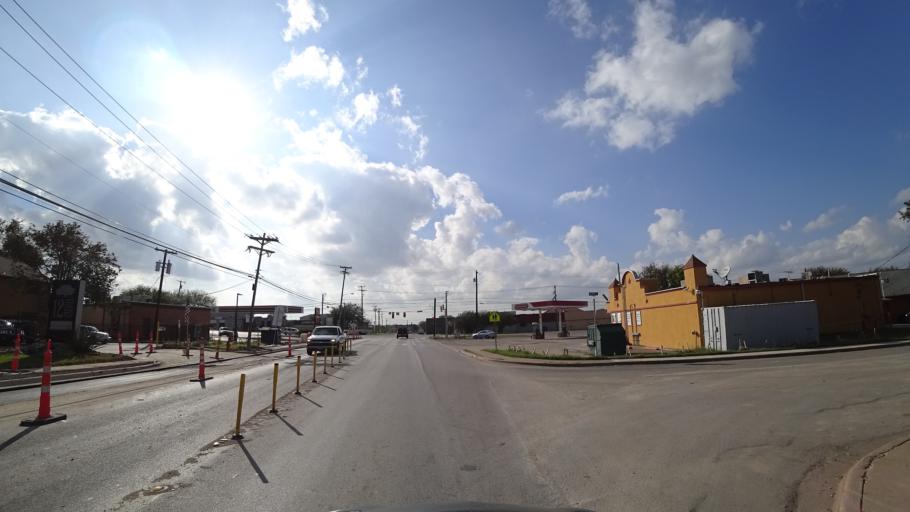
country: US
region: Texas
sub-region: Williamson County
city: Round Rock
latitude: 30.4938
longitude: -97.6749
